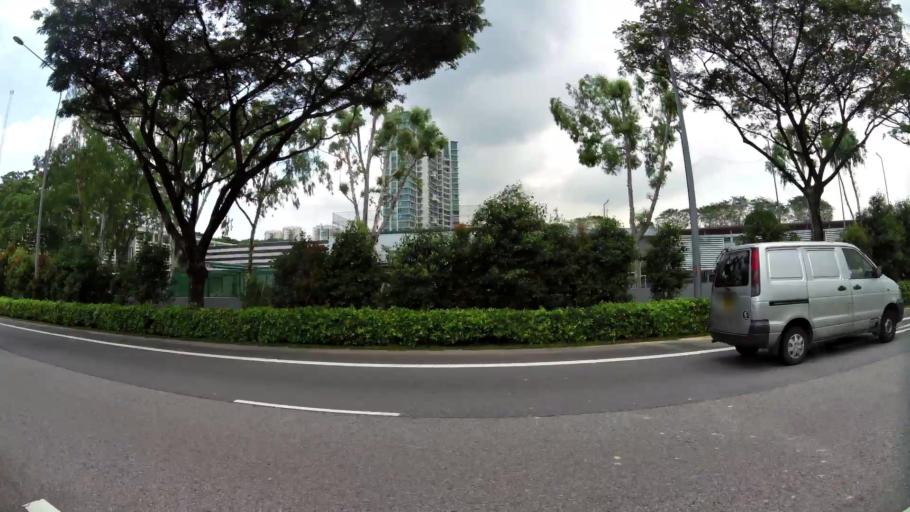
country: SG
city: Singapore
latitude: 1.3488
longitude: 103.8586
